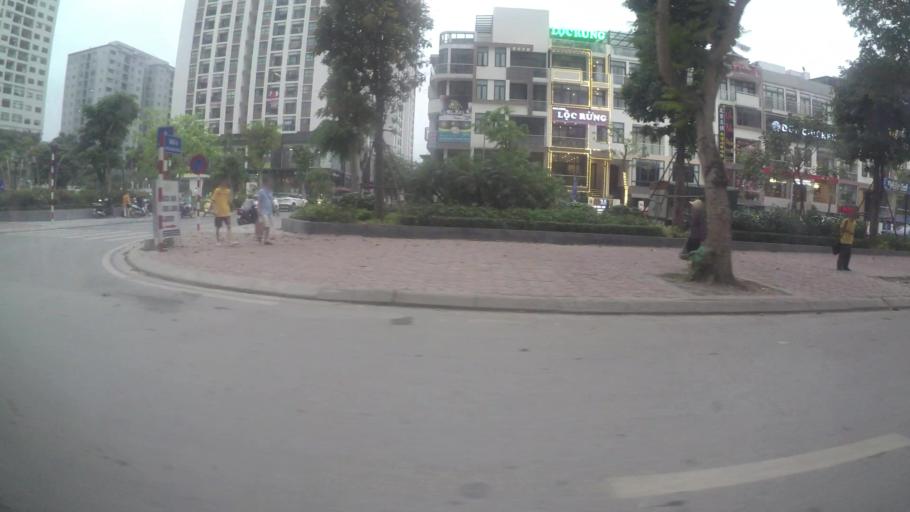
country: VN
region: Ha Noi
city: Cau Dien
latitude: 21.0343
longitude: 105.7668
